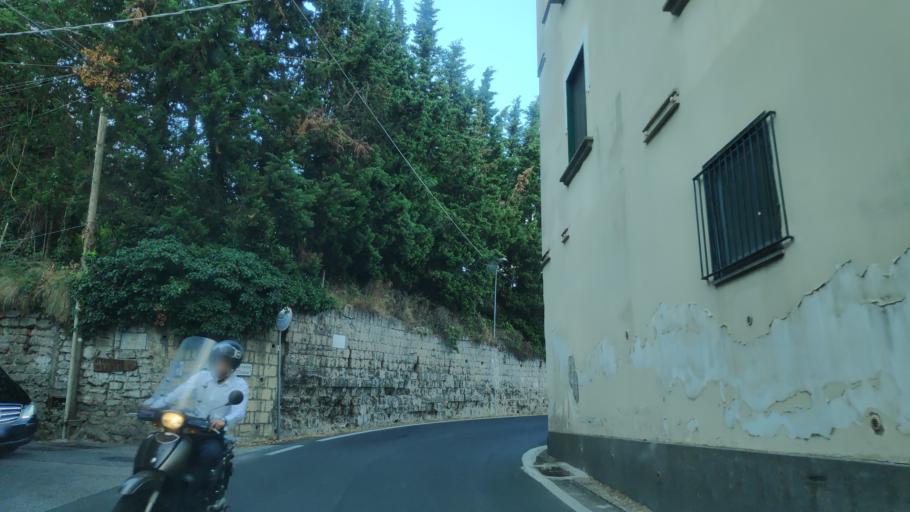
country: IT
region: Campania
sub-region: Provincia di Napoli
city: Piano di Sorrento
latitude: 40.6286
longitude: 14.4239
